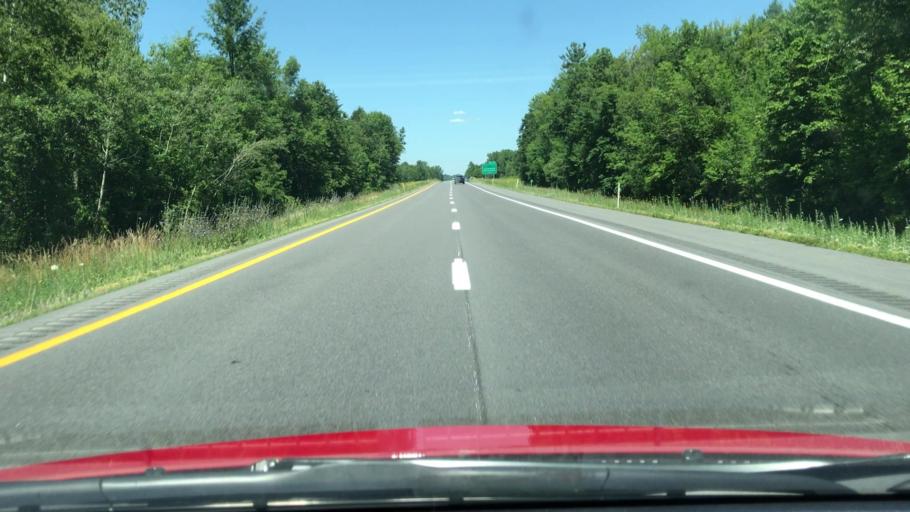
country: US
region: New York
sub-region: Clinton County
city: Cumberland Head
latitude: 44.7601
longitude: -73.4301
